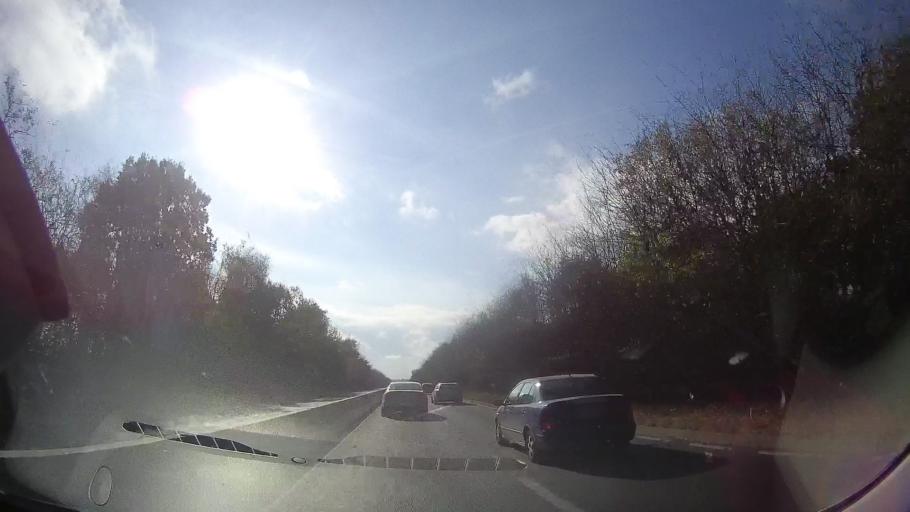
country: RO
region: Constanta
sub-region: Comuna Agigea
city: Agigea
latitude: 44.1271
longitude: 28.6154
